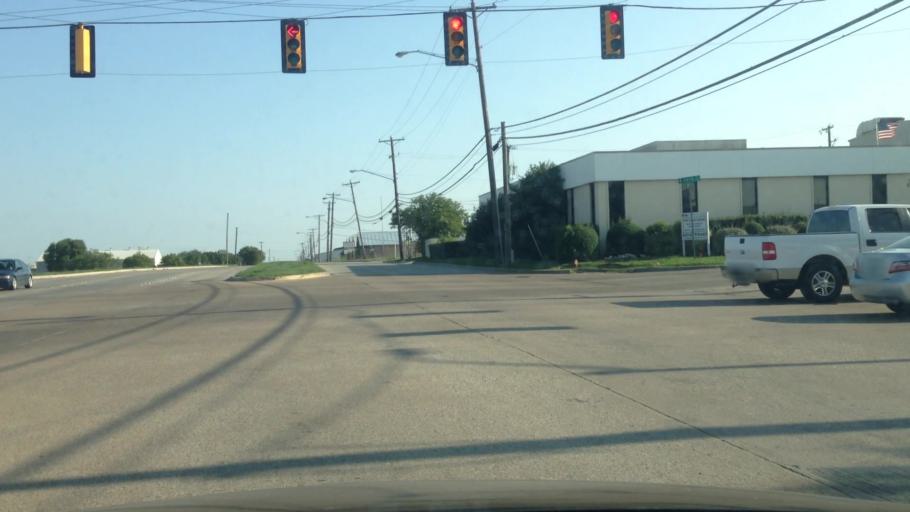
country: US
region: Texas
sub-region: Tarrant County
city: Haltom City
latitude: 32.8108
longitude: -97.3084
